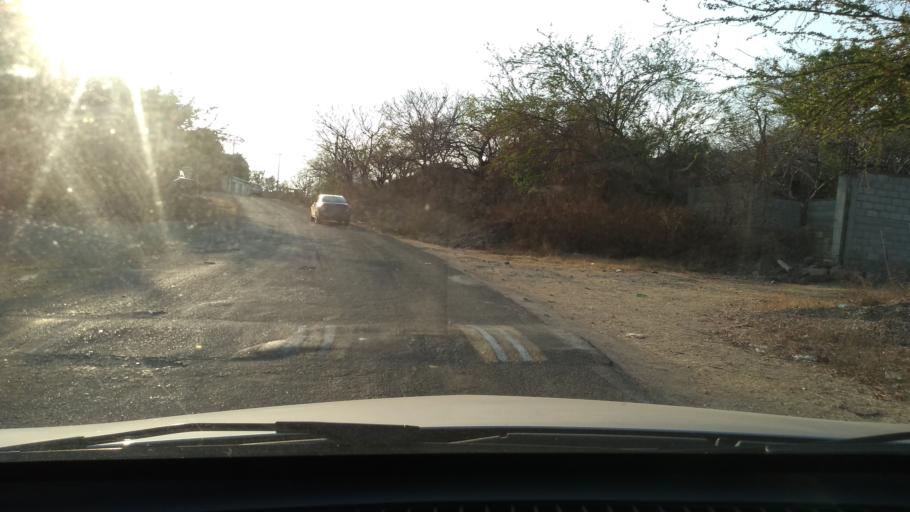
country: MX
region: Morelos
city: Puente de Ixtla
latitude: 18.6047
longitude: -99.3131
